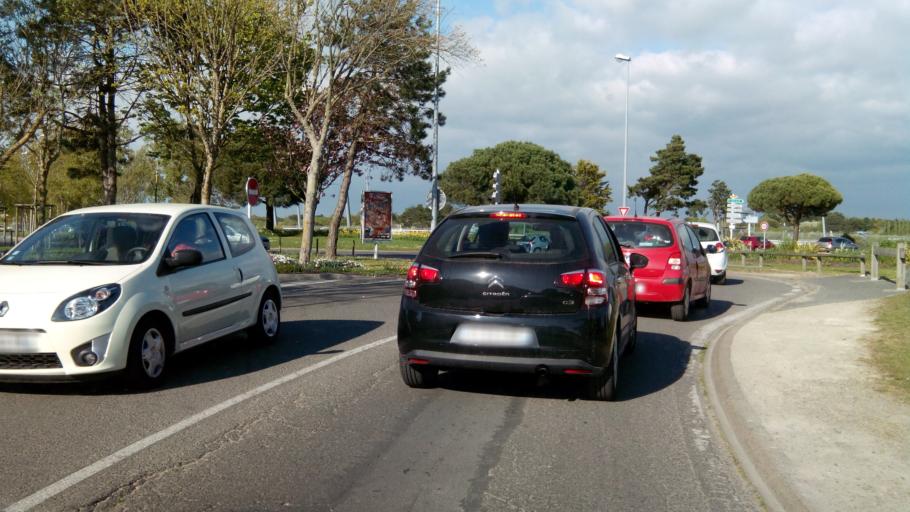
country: FR
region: Pays de la Loire
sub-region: Departement de la Loire-Atlantique
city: Pornichet
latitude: 47.2603
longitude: -2.3348
